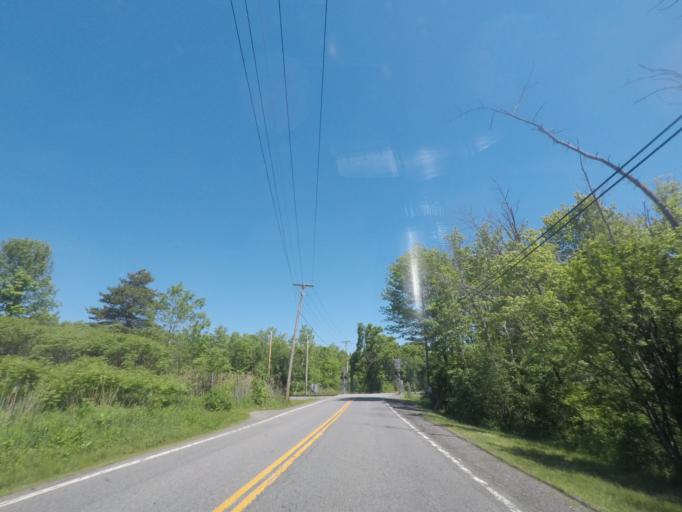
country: US
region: New York
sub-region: Schenectady County
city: East Glenville
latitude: 42.8852
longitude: -73.8647
